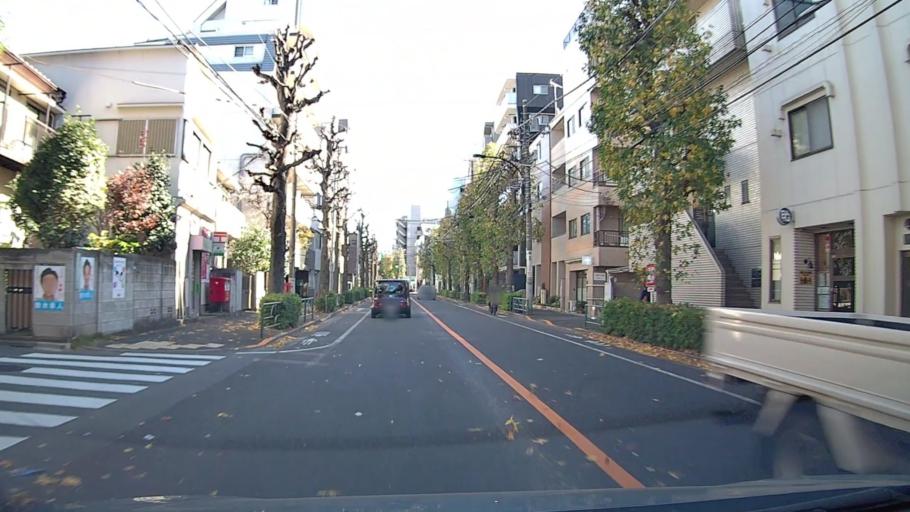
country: JP
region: Tokyo
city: Tokyo
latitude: 35.7250
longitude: 139.6445
